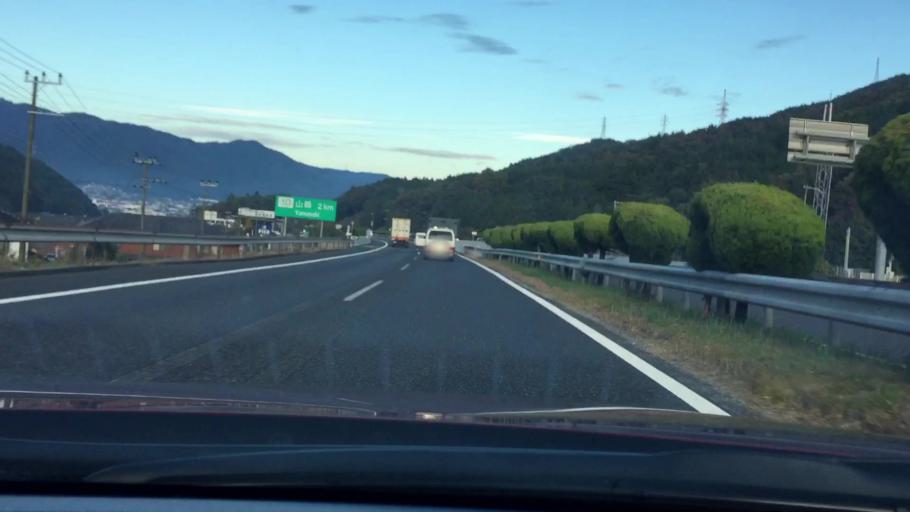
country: JP
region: Hyogo
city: Yamazakicho-nakabirose
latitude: 34.9934
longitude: 134.5725
